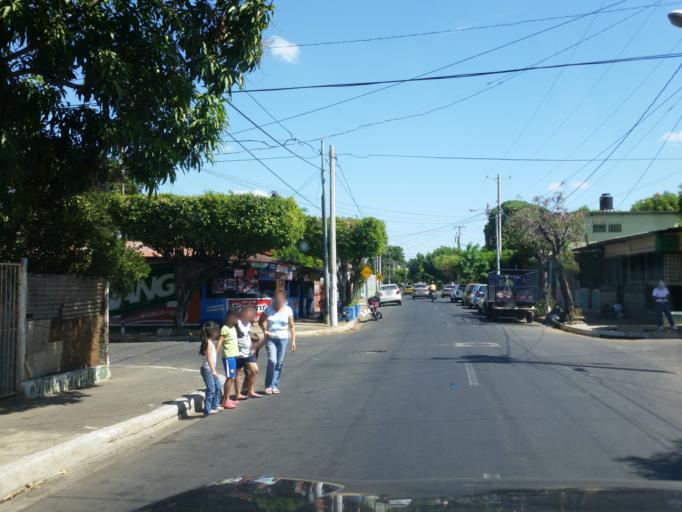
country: NI
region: Managua
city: Ciudad Sandino
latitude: 12.1495
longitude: -86.3012
